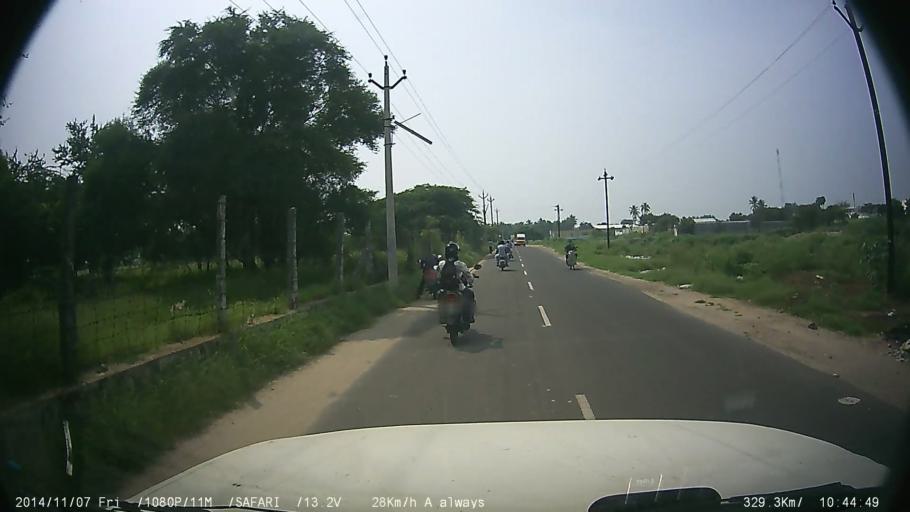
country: IN
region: Tamil Nadu
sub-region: Tiruppur
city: Tiruppur
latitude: 11.1028
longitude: 77.3142
